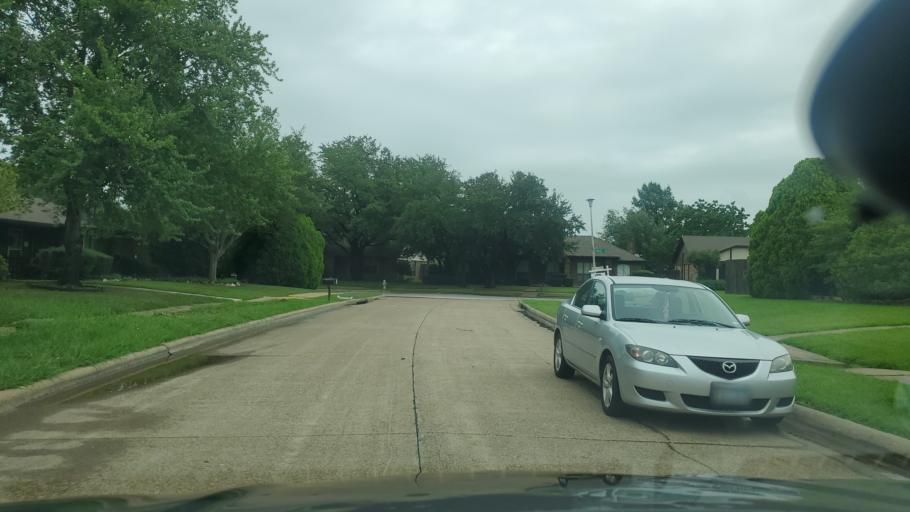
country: US
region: Texas
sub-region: Dallas County
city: Garland
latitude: 32.9383
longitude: -96.6309
